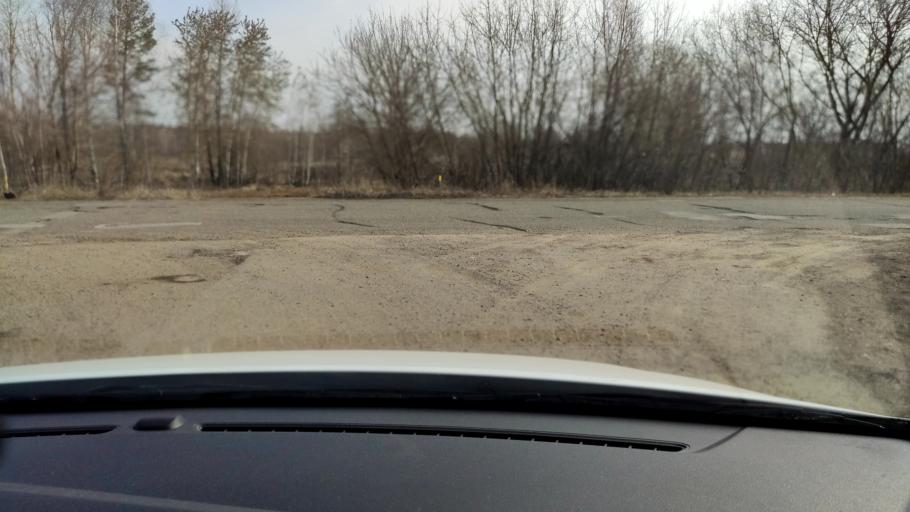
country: RU
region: Tatarstan
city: Stolbishchi
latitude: 55.7171
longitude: 49.2192
